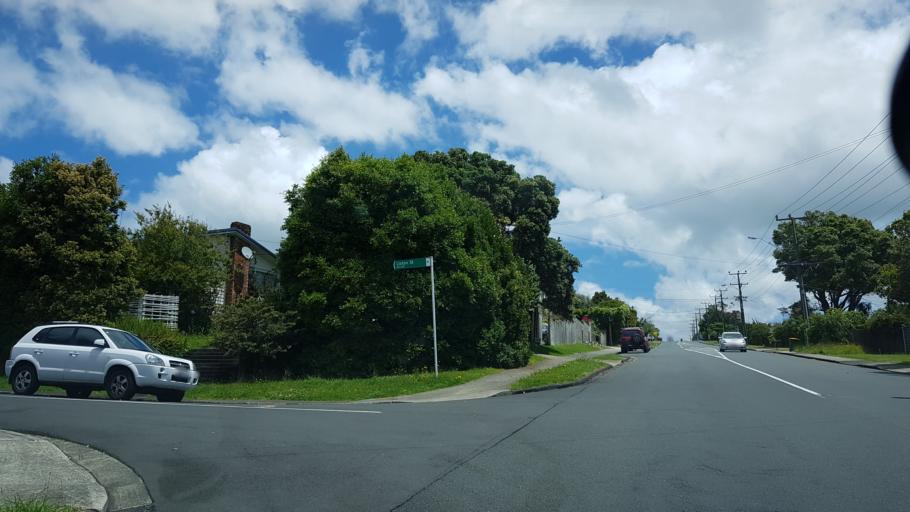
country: NZ
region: Auckland
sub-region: Auckland
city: North Shore
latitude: -36.7965
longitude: 174.7422
